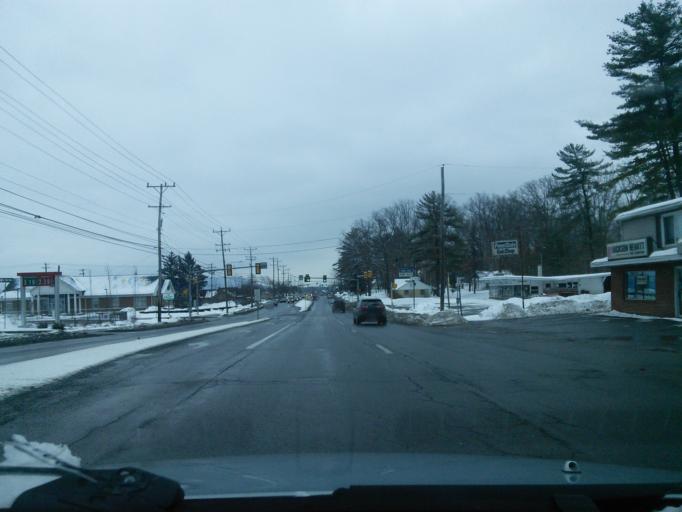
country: US
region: Pennsylvania
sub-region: Centre County
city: Park Forest Village
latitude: 40.8087
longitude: -77.9015
